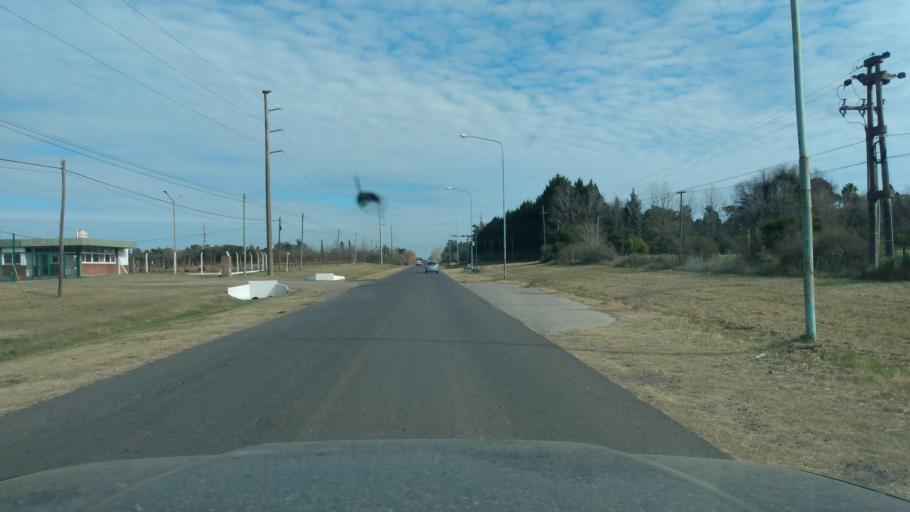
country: AR
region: Buenos Aires
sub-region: Partido de Lujan
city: Lujan
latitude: -34.5690
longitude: -59.1506
